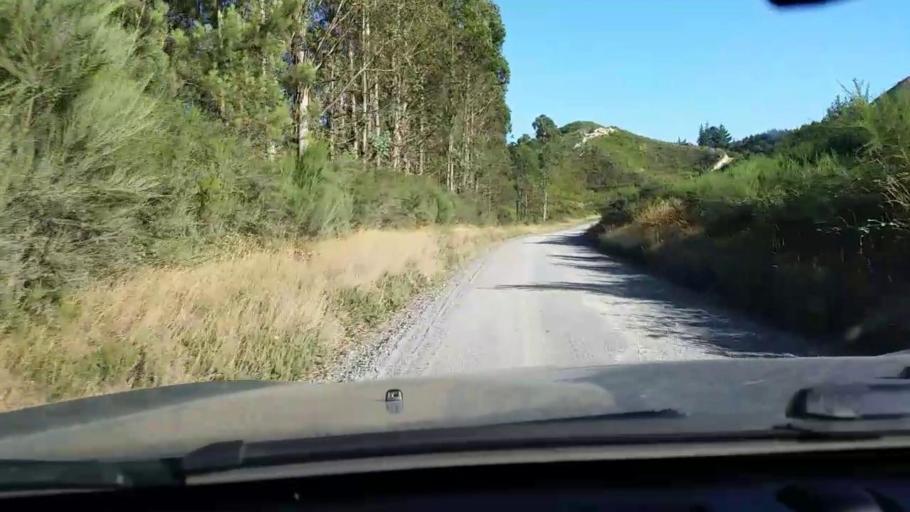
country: NZ
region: Waikato
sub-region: Taupo District
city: Taupo
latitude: -38.4625
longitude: 176.1600
